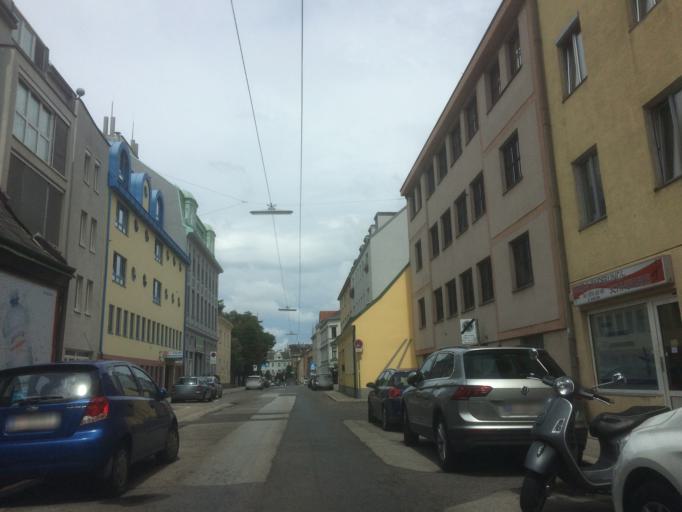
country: AT
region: Lower Austria
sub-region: Politischer Bezirk Modling
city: Perchtoldsdorf
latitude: 48.1886
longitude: 16.2858
